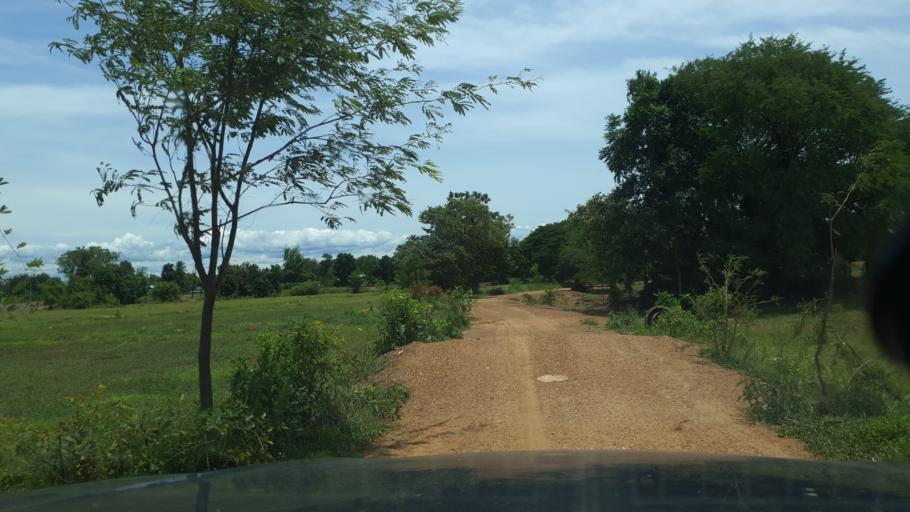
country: TH
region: Sukhothai
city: Ban Na
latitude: 17.0828
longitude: 99.6902
